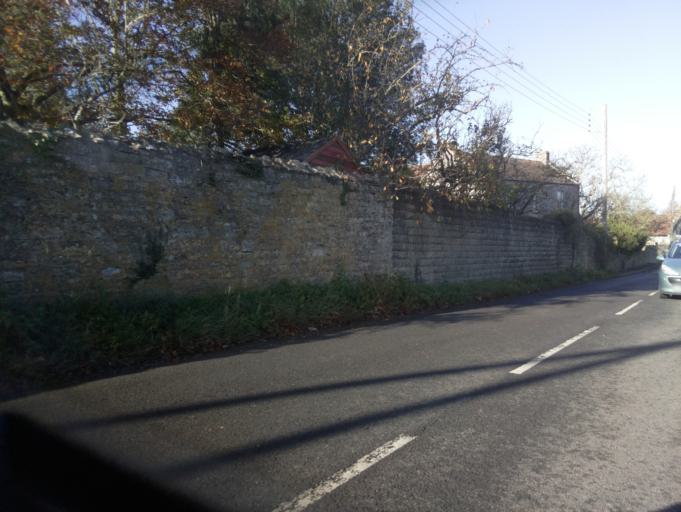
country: GB
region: England
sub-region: Somerset
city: Martock
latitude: 51.0233
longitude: -2.7585
